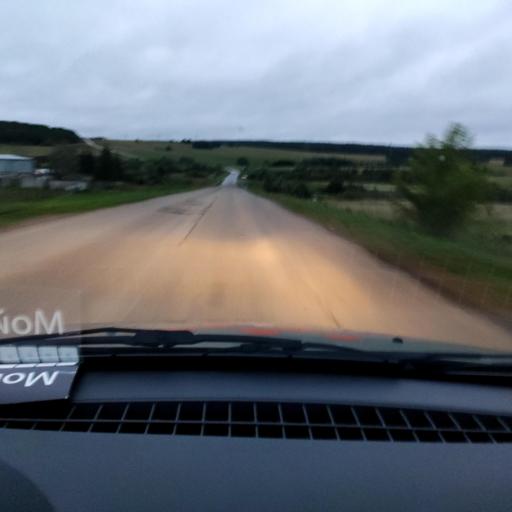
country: RU
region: Bashkortostan
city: Iglino
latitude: 54.8794
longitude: 56.5733
